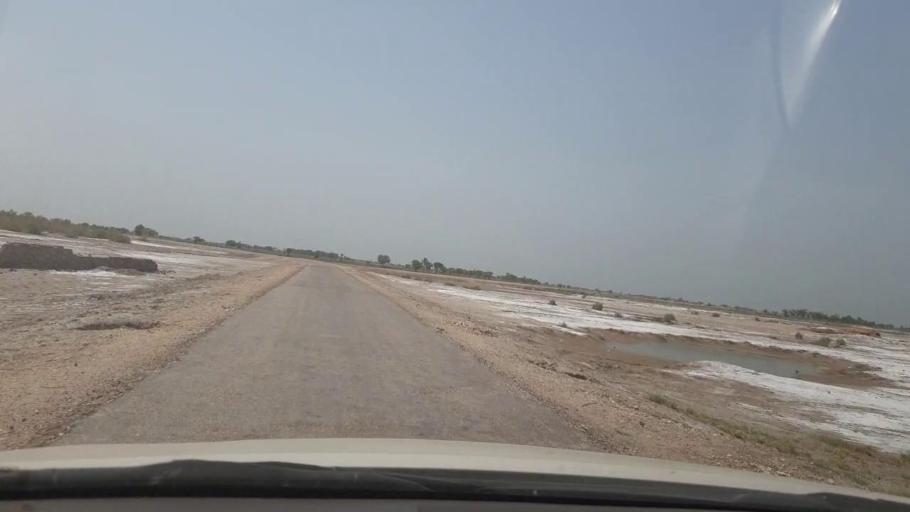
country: PK
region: Sindh
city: Shikarpur
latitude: 27.9928
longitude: 68.5643
